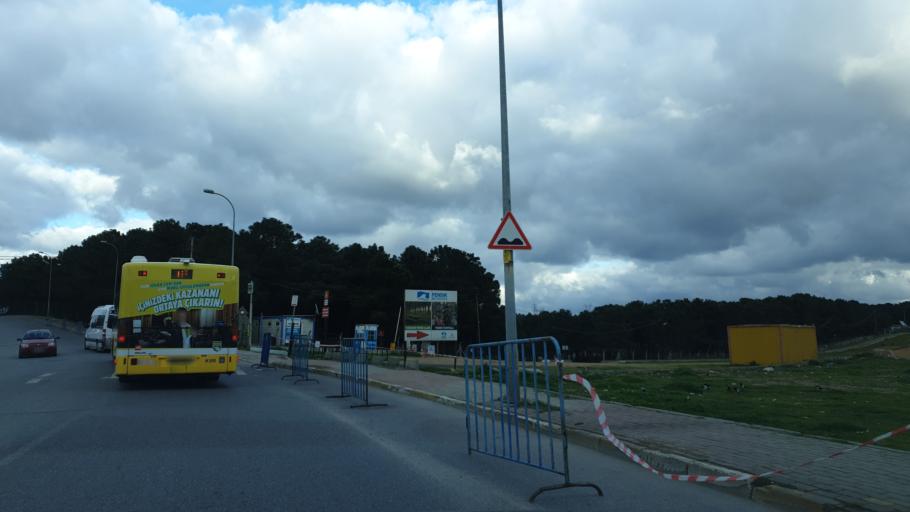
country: TR
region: Istanbul
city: Sultanbeyli
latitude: 40.9449
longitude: 29.3053
